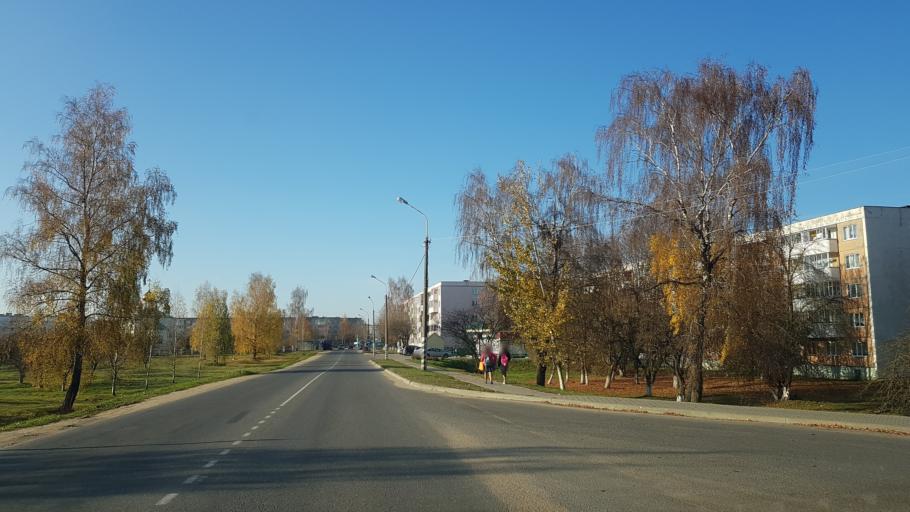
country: BY
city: Fanipol
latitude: 53.7377
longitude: 27.3201
